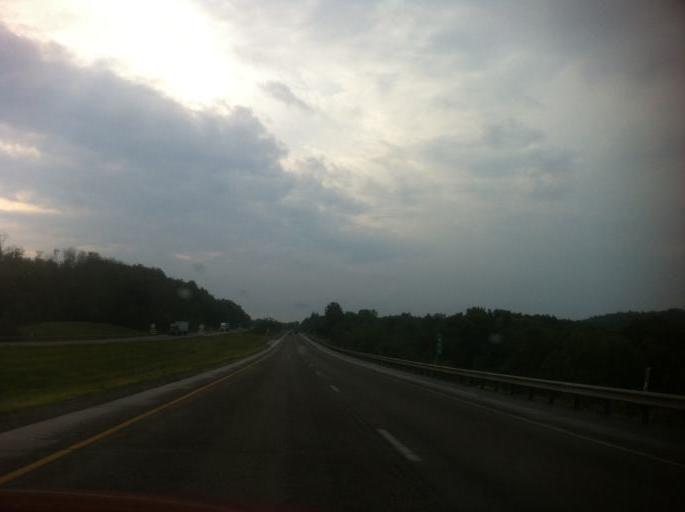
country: US
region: Pennsylvania
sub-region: Clarion County
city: Knox
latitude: 41.1913
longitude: -79.6129
